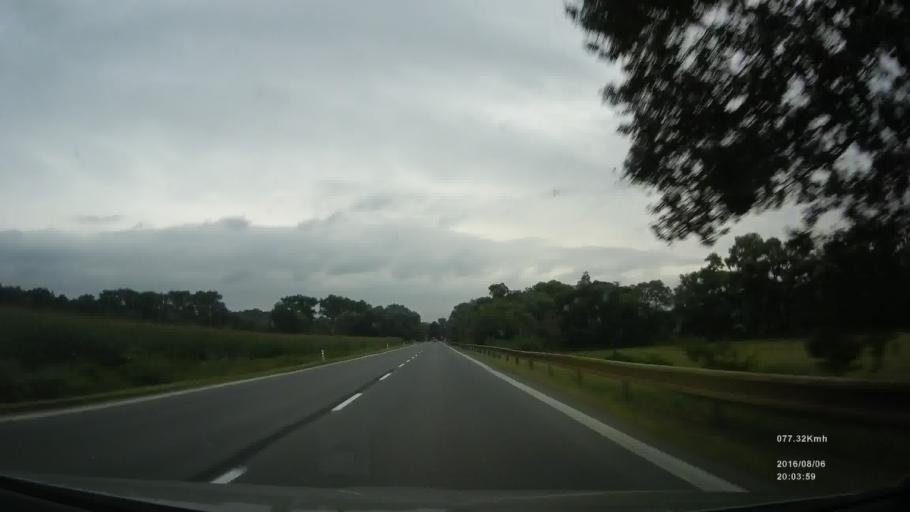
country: SK
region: Presovsky
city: Stropkov
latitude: 49.2448
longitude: 21.6169
